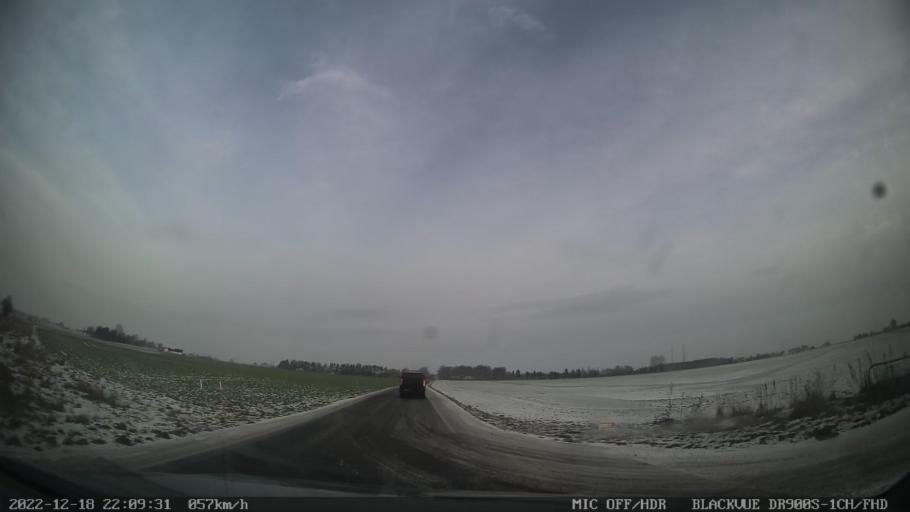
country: SE
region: Skane
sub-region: Tomelilla Kommun
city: Tomelilla
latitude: 55.5344
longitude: 14.0416
